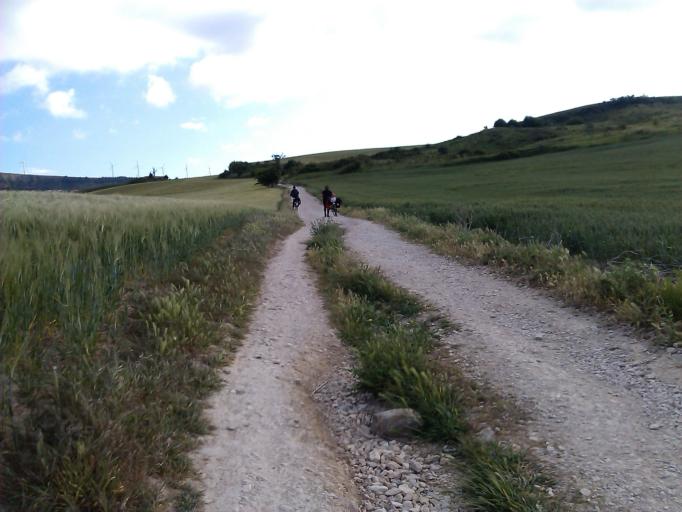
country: ES
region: Navarre
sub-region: Provincia de Navarra
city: Galar
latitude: 42.7549
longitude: -1.7166
